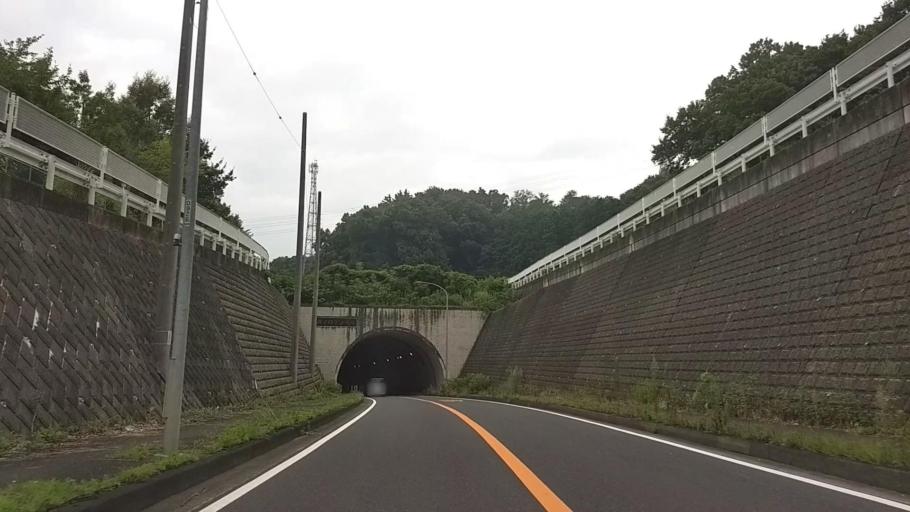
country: JP
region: Kanagawa
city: Hadano
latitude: 35.3394
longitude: 139.2276
